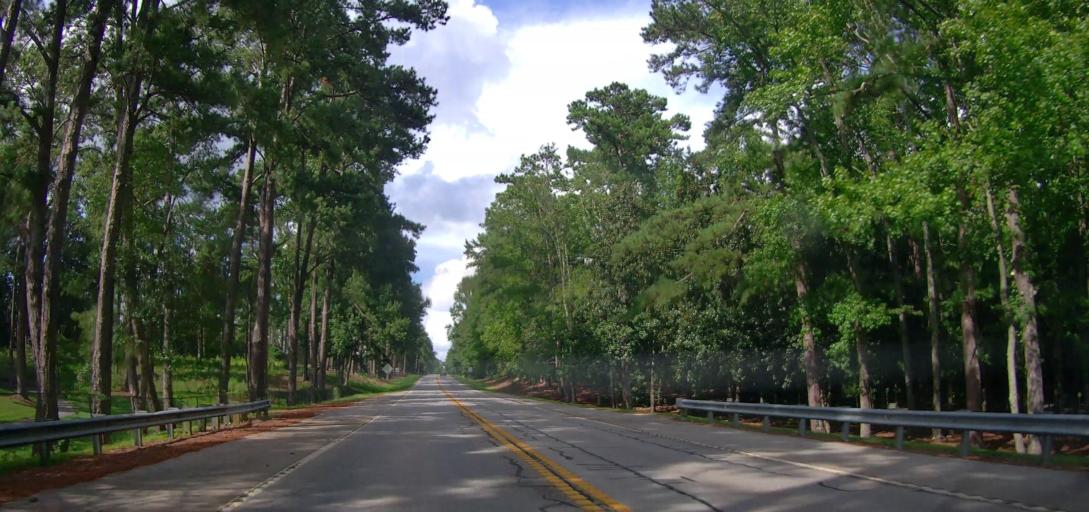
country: US
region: Georgia
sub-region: Harris County
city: Pine Mountain
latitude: 32.8330
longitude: -84.8437
